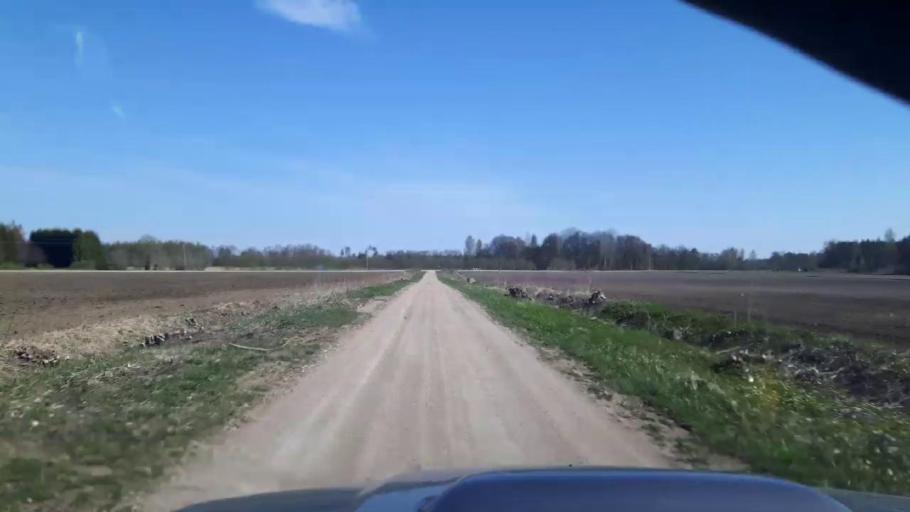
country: EE
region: Paernumaa
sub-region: Tootsi vald
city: Tootsi
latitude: 58.5235
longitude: 24.9296
